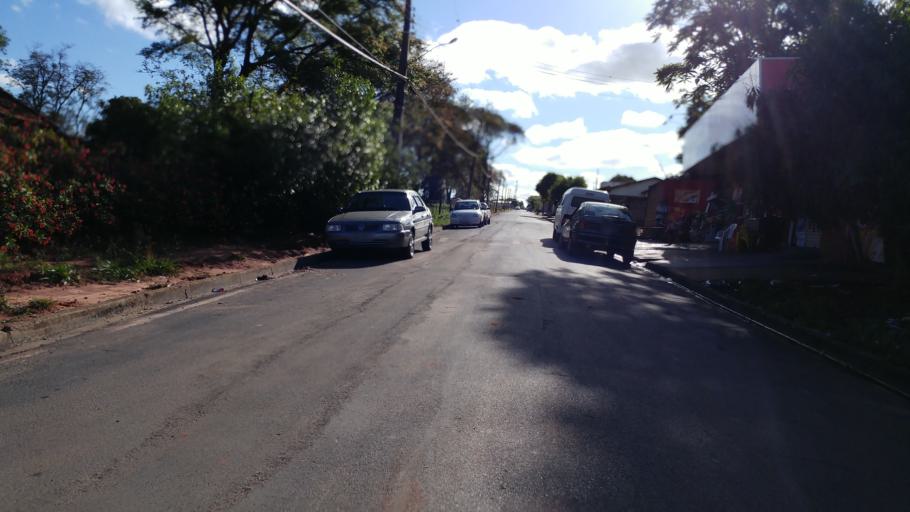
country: BR
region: Sao Paulo
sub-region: Paraguacu Paulista
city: Paraguacu Paulista
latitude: -22.4338
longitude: -50.5763
